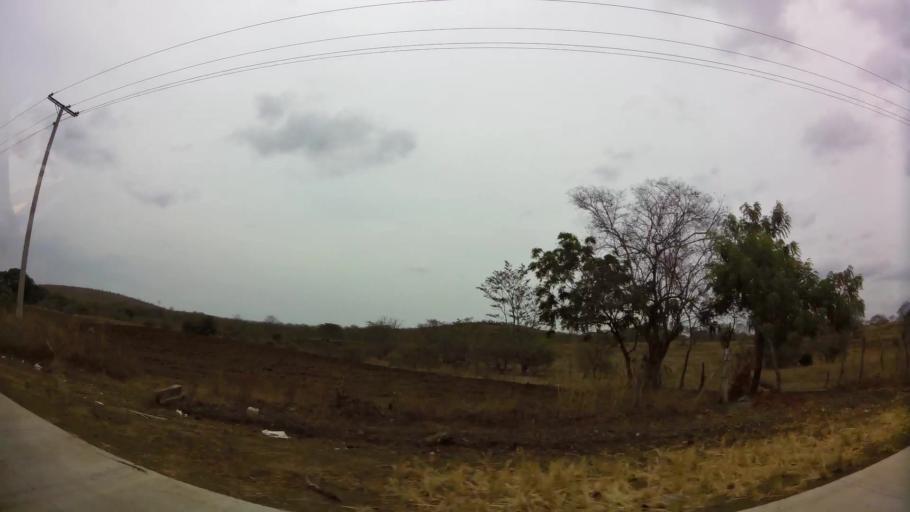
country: NI
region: Masaya
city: Ticuantepe
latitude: 12.0961
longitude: -86.1773
